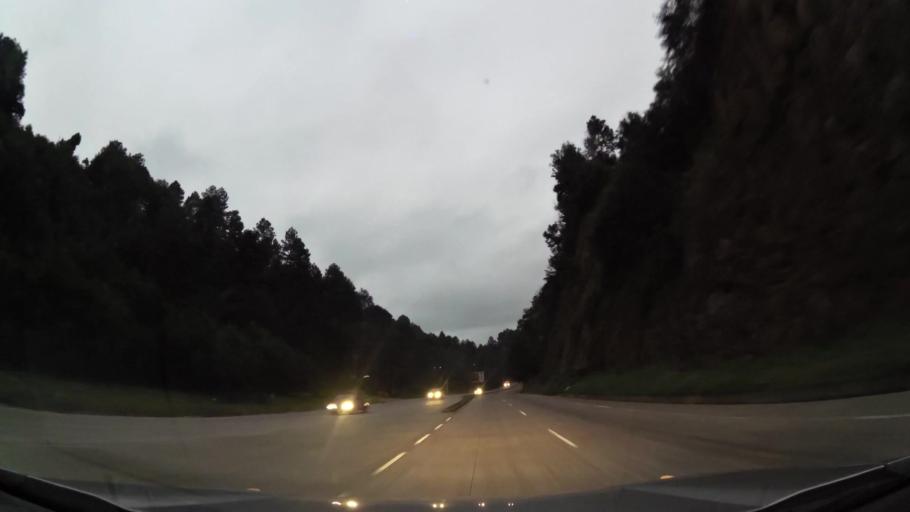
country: GT
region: Chimaltenango
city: Tecpan Guatemala
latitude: 14.8274
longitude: -91.0374
